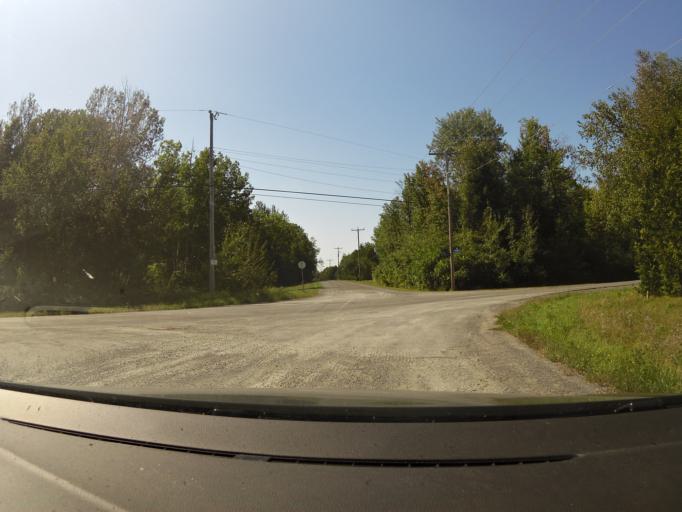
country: CA
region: Ontario
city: Bells Corners
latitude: 45.2898
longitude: -75.9907
